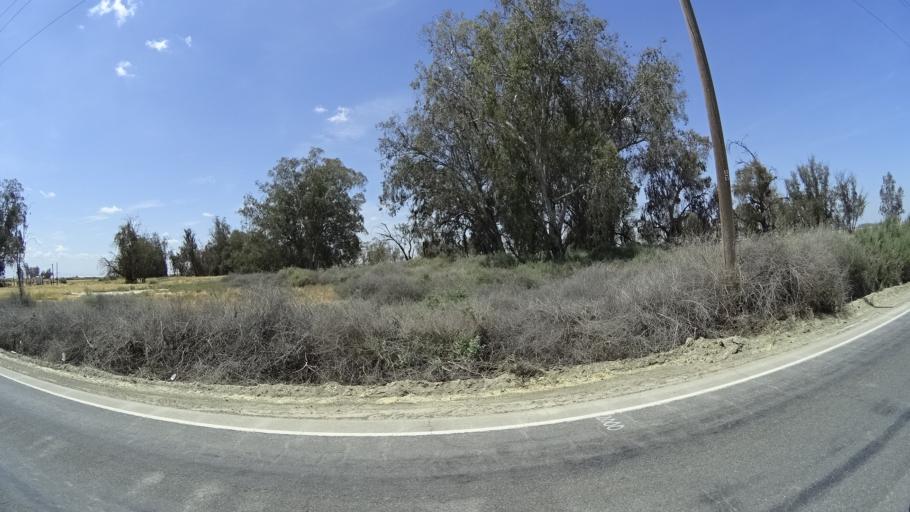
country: US
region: California
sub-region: Kings County
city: Home Garden
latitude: 36.2169
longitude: -119.6547
